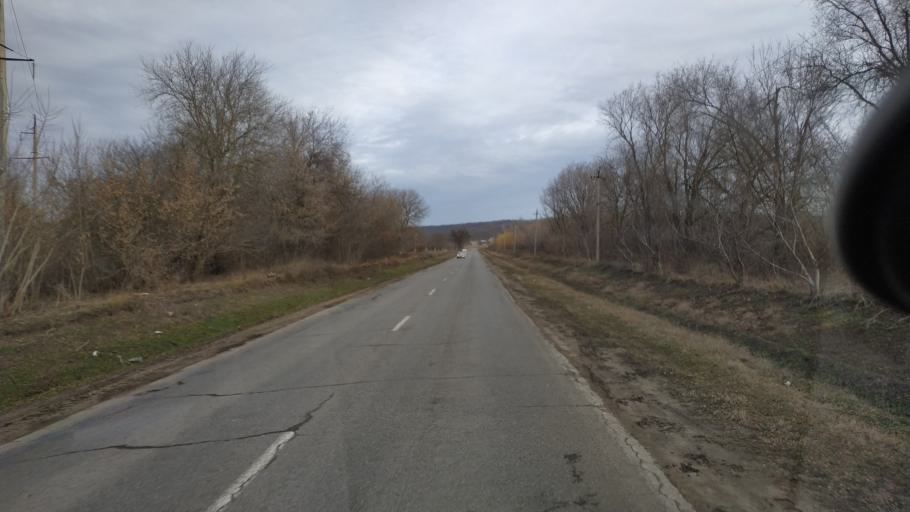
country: MD
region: Chisinau
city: Vadul lui Voda
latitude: 47.1318
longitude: 29.0620
